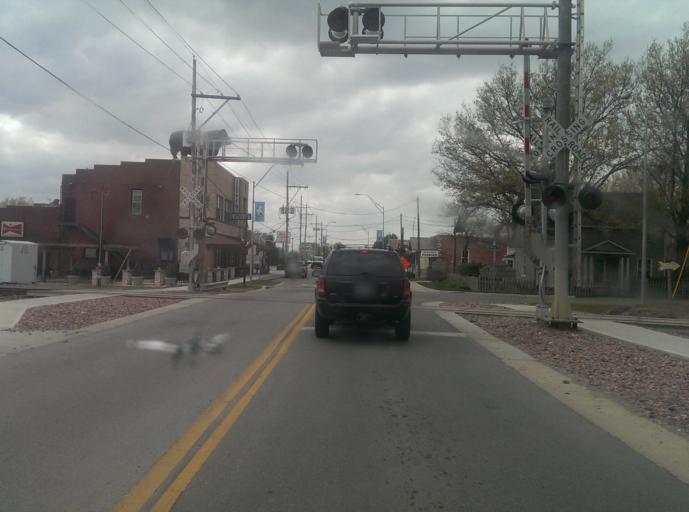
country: US
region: Missouri
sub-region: Jackson County
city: Grandview
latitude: 38.8825
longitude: -94.5884
